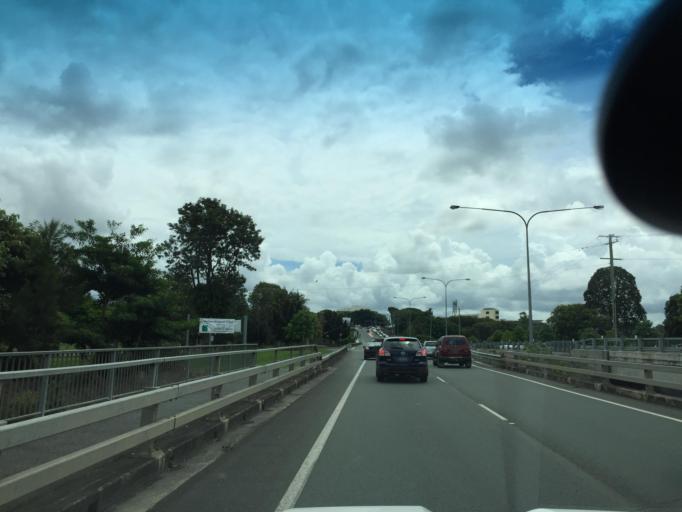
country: AU
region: Queensland
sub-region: Moreton Bay
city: Caboolture South
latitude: -27.0898
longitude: 152.9503
